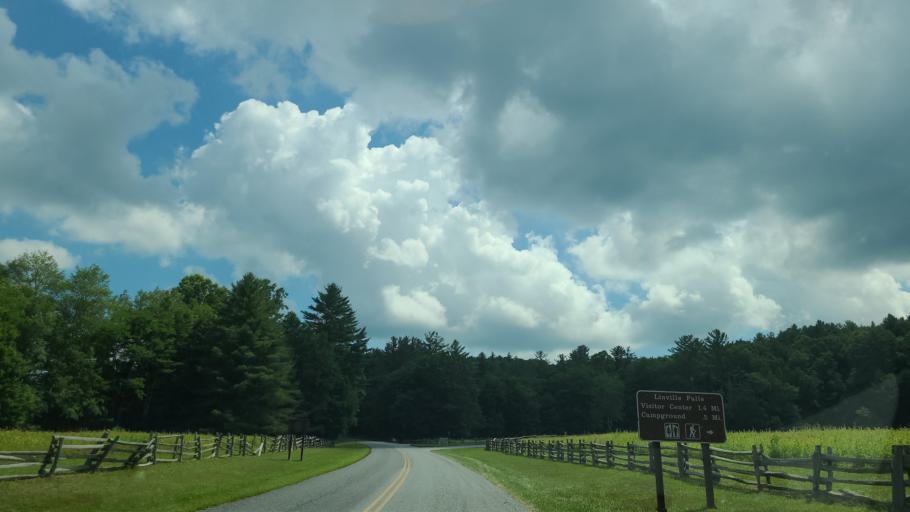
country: US
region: North Carolina
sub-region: Avery County
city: Newland
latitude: 35.9743
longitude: -81.9349
